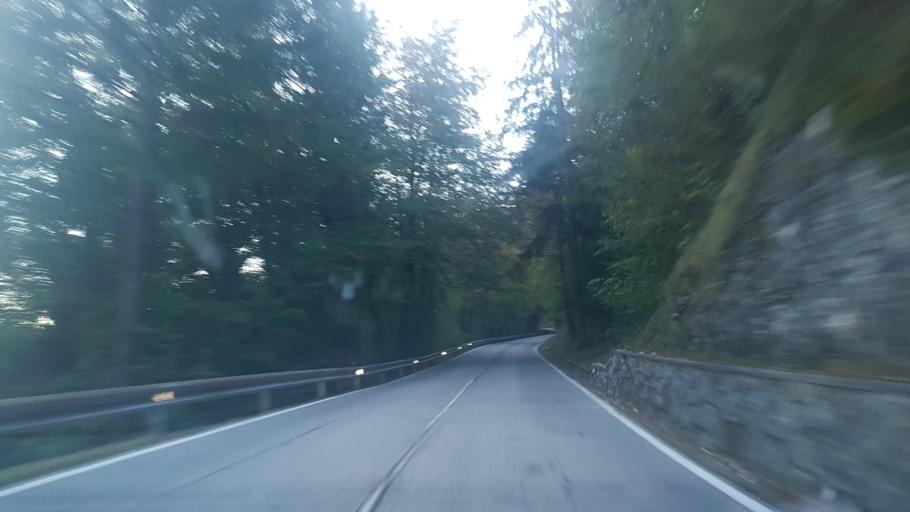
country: IT
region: Friuli Venezia Giulia
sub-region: Provincia di Udine
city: Chiaulis
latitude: 46.3814
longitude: 12.9592
